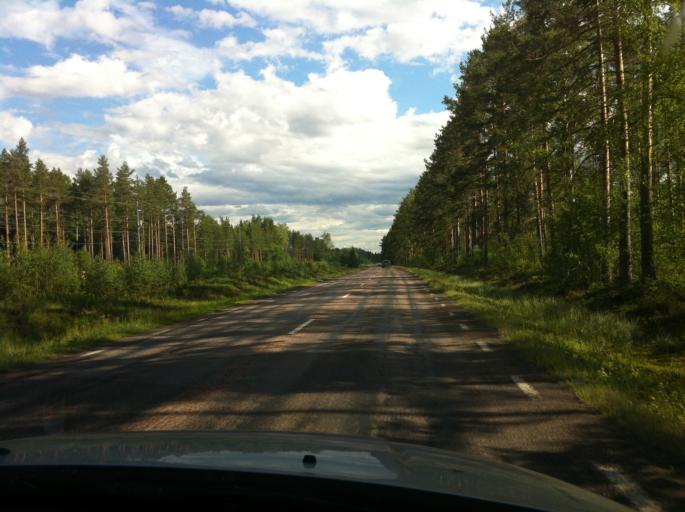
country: SE
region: Gaevleborg
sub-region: Ockelbo Kommun
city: Ockelbo
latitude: 60.8554
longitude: 16.7017
